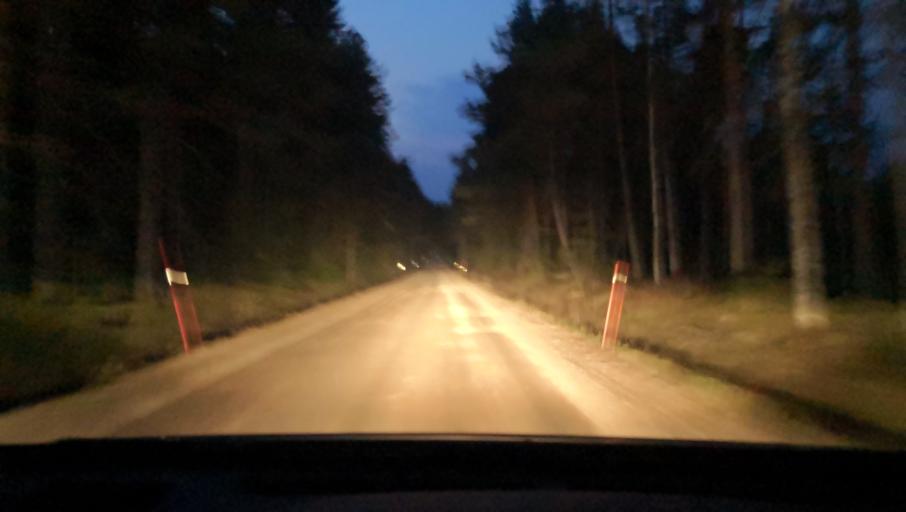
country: SE
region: OErebro
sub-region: Lindesbergs Kommun
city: Frovi
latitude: 59.6346
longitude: 15.4726
